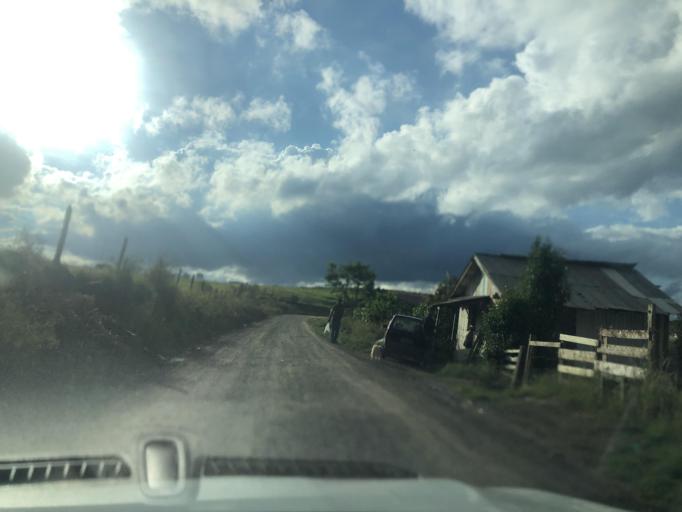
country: BR
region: Santa Catarina
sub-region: Lages
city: Lages
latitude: -27.7912
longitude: -50.3234
